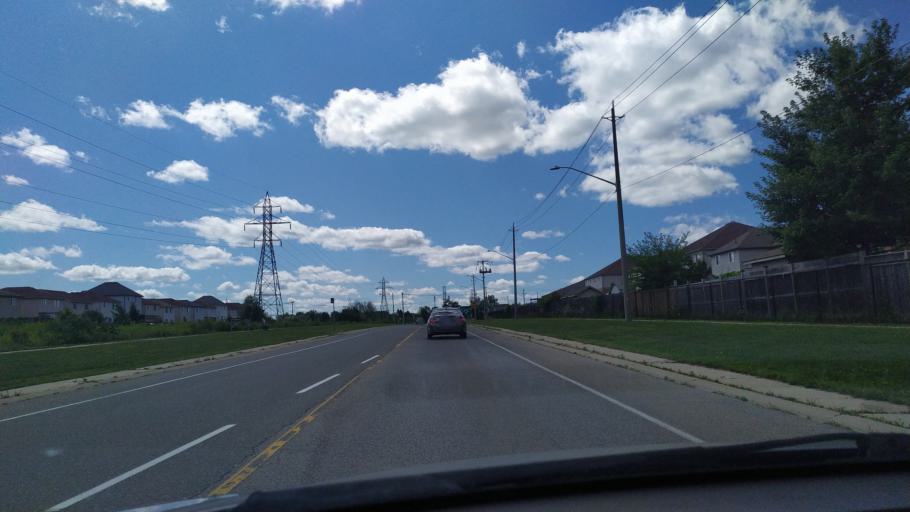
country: CA
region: Ontario
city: Kitchener
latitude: 43.4297
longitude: -80.5500
